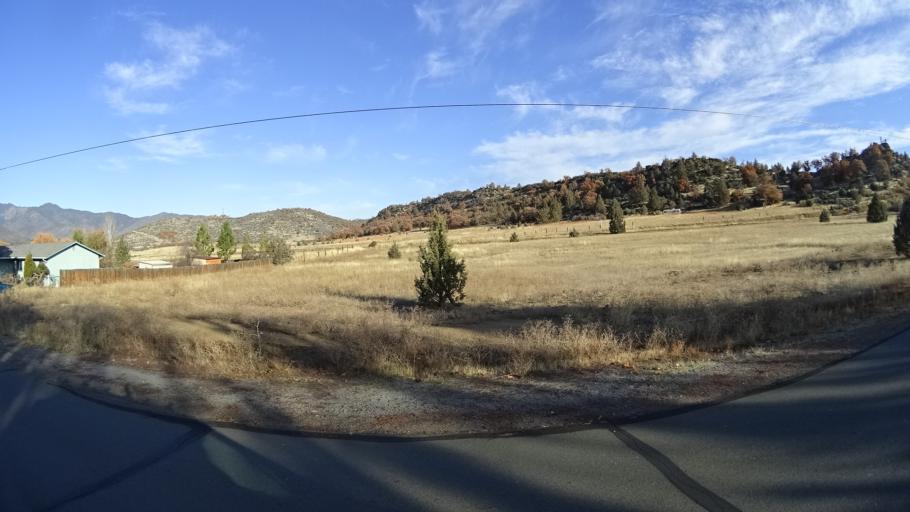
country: US
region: California
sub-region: Siskiyou County
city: Yreka
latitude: 41.7114
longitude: -122.6180
